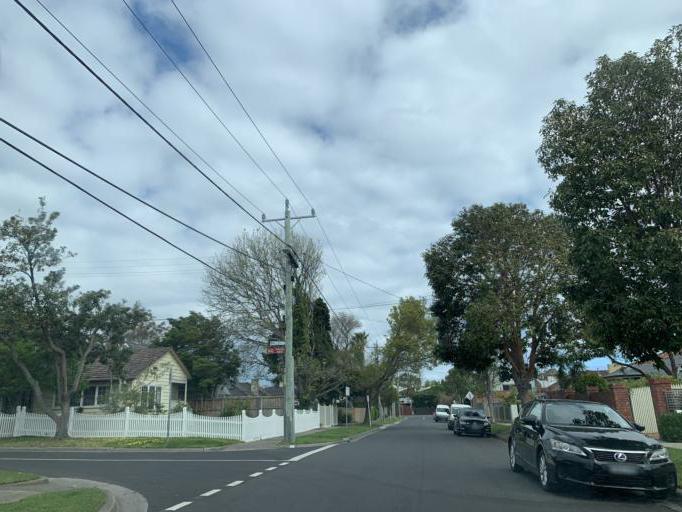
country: AU
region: Victoria
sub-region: Bayside
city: Cheltenham
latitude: -37.9778
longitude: 145.0468
